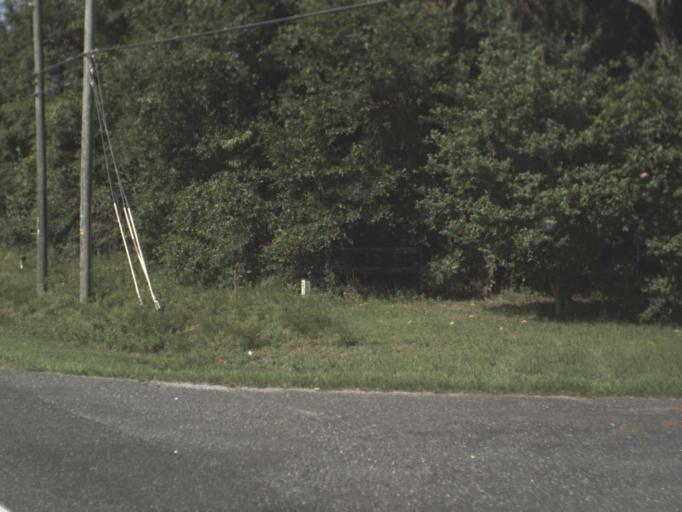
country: US
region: Florida
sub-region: Alachua County
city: High Springs
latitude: 29.9292
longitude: -82.7140
